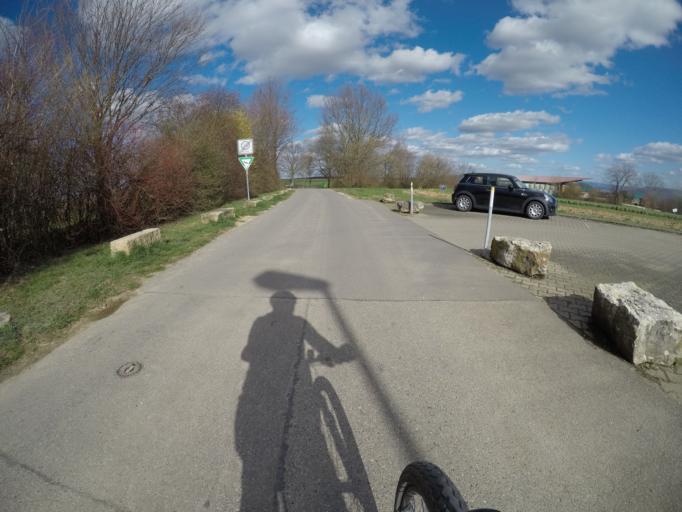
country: DE
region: Baden-Wuerttemberg
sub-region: Regierungsbezirk Stuttgart
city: Wolfschlugen
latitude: 48.6547
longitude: 9.2530
